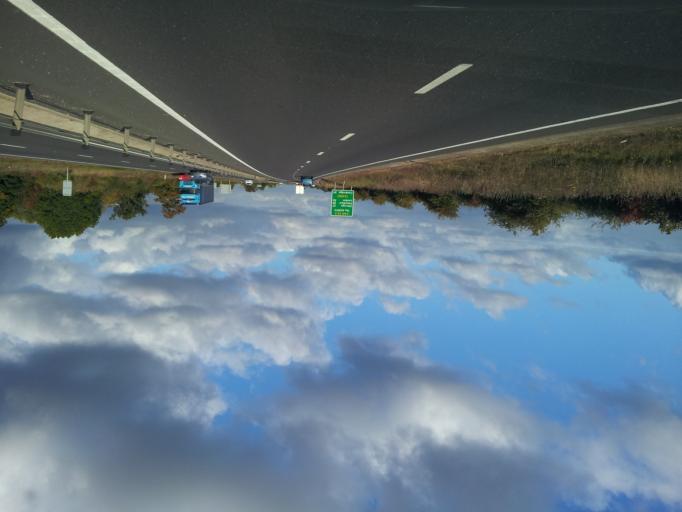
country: GB
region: England
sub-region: Bedford
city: Willington
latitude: 52.1560
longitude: -0.3792
